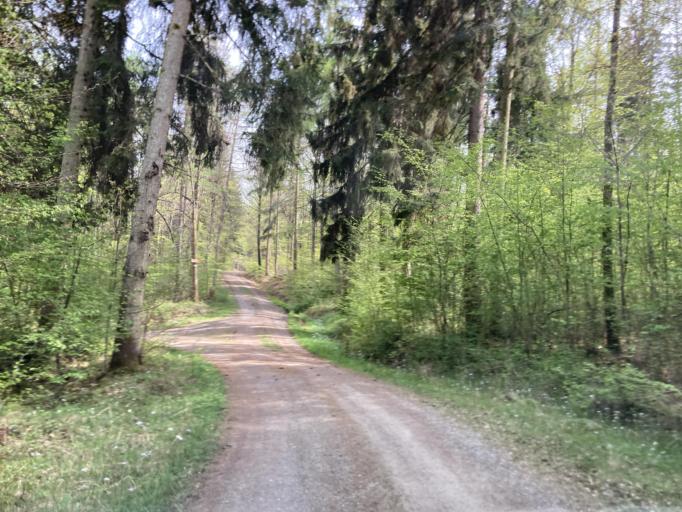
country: DE
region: Baden-Wuerttemberg
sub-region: Tuebingen Region
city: Rottenburg
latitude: 48.4568
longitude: 8.9828
